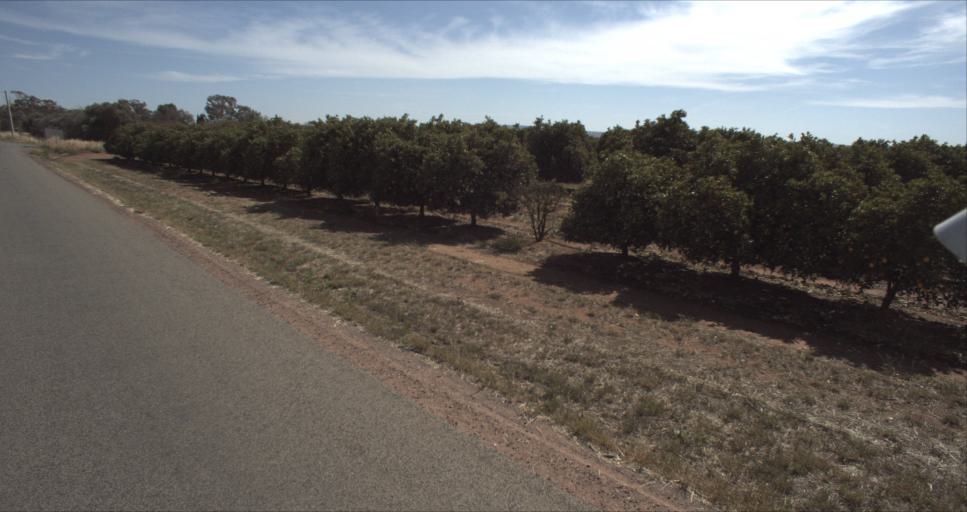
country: AU
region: New South Wales
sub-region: Leeton
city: Leeton
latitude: -34.5791
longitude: 146.4683
